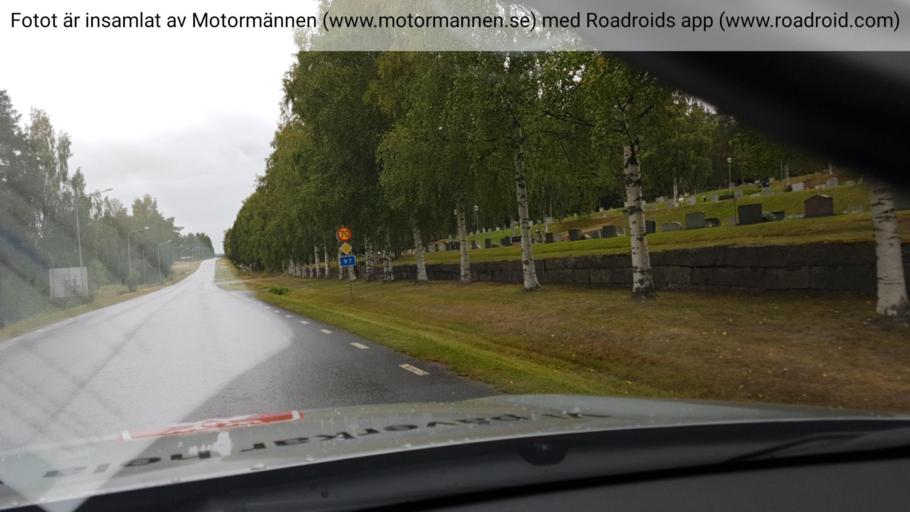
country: SE
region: Norrbotten
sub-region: Alvsbyns Kommun
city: AElvsbyn
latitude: 66.0889
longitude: 20.9481
